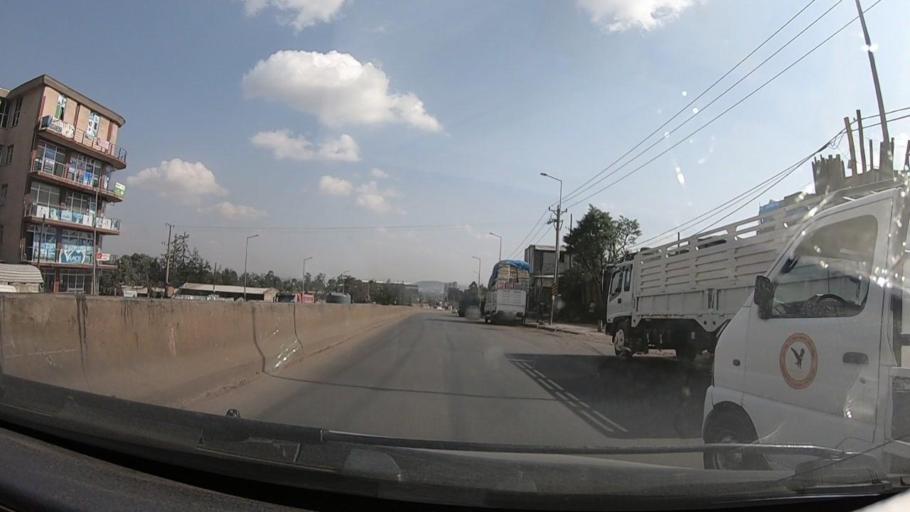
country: ET
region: Adis Abeba
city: Addis Ababa
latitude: 8.9880
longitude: 38.6927
